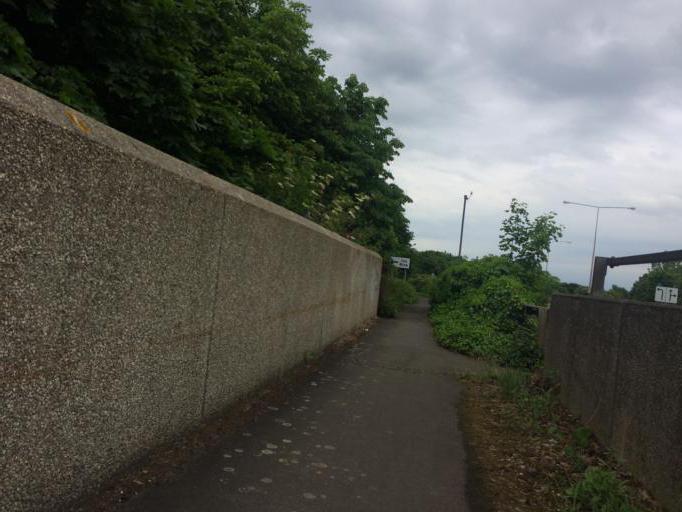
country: GB
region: England
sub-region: Milton Keynes
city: Loughton
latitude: 52.0309
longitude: -0.7700
